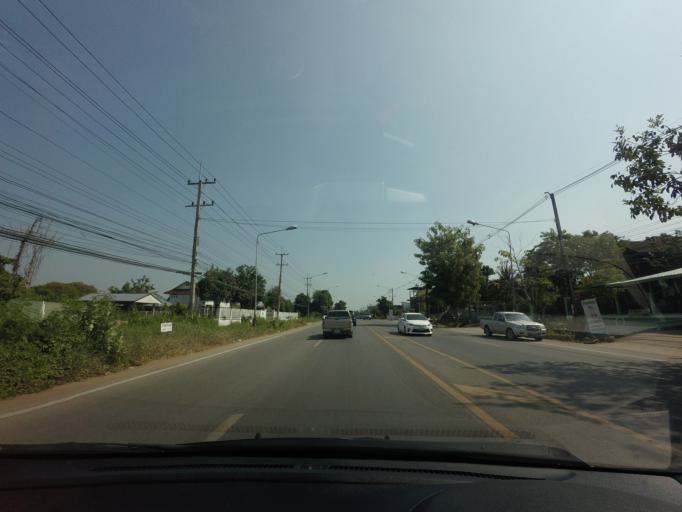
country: TH
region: Sukhothai
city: Sukhothai
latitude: 17.0110
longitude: 99.7837
